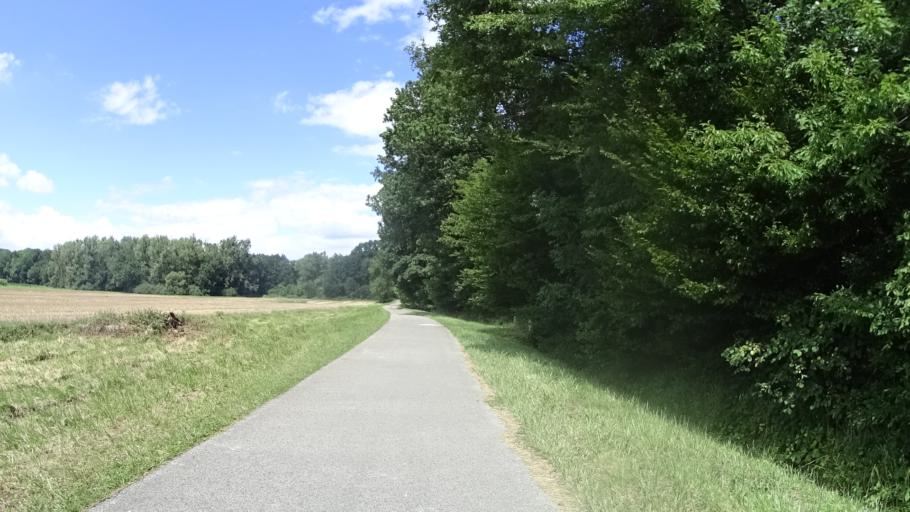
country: FR
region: Champagne-Ardenne
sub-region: Departement de la Haute-Marne
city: Montier-en-Der
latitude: 48.5221
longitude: 4.7714
